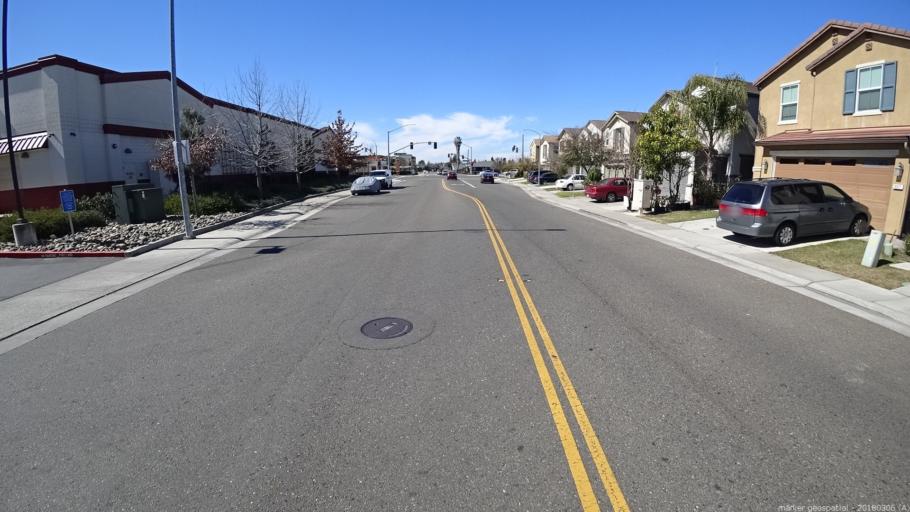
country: US
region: California
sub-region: Sacramento County
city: Vineyard
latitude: 38.4562
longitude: -121.3707
